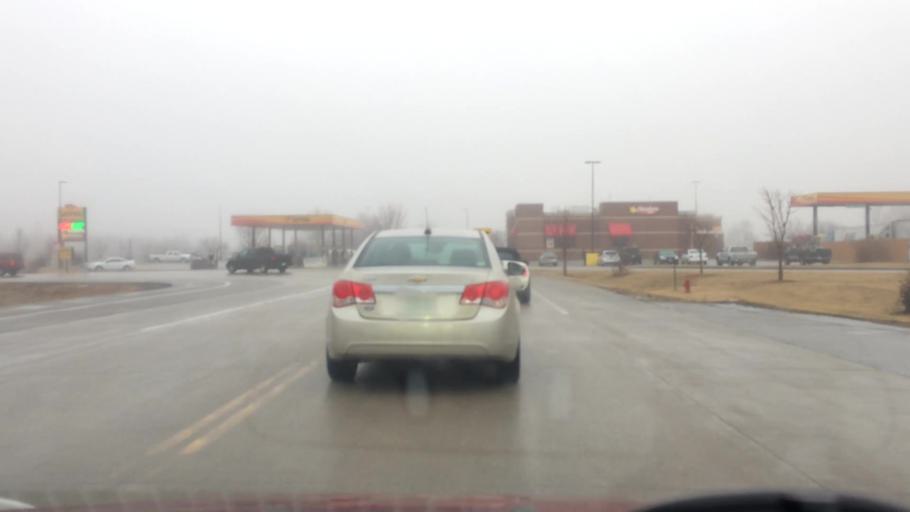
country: US
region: Missouri
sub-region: Greene County
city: Strafford
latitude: 37.2752
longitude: -93.1125
